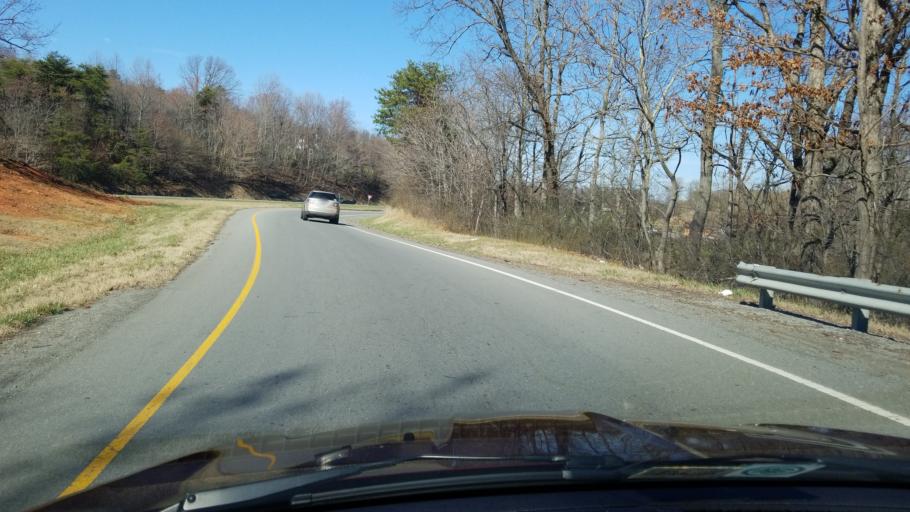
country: US
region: Virginia
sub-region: Franklin County
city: Rocky Mount
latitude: 37.0236
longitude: -79.8809
